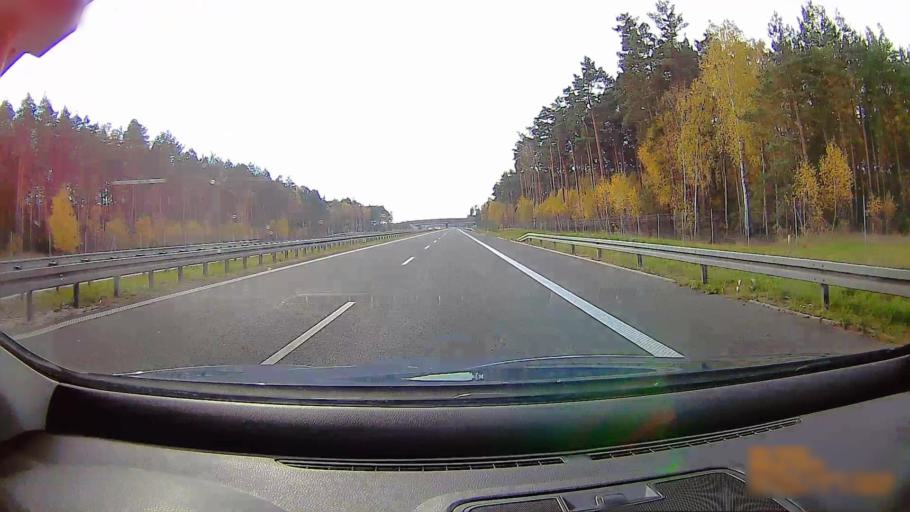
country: PL
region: Greater Poland Voivodeship
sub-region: Powiat ostrowski
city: Przygodzice
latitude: 51.5662
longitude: 17.8473
